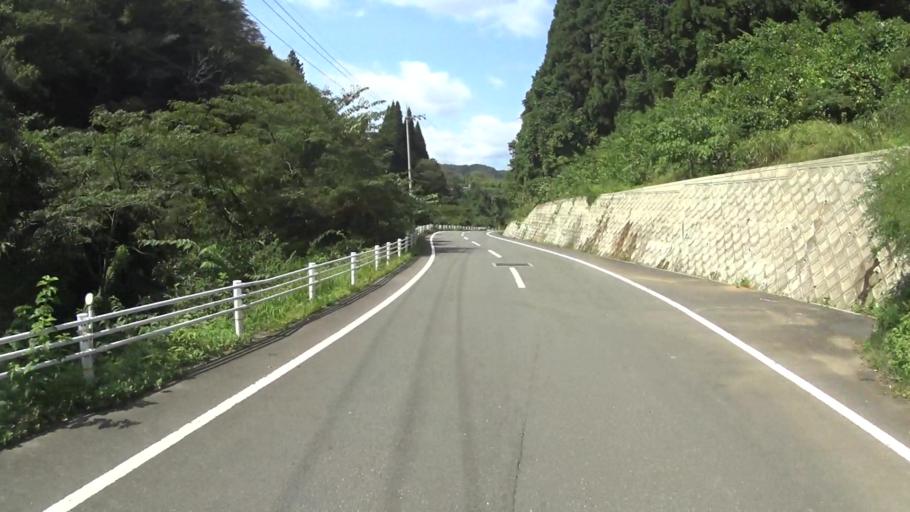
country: JP
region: Kyoto
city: Miyazu
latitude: 35.6845
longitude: 135.2605
